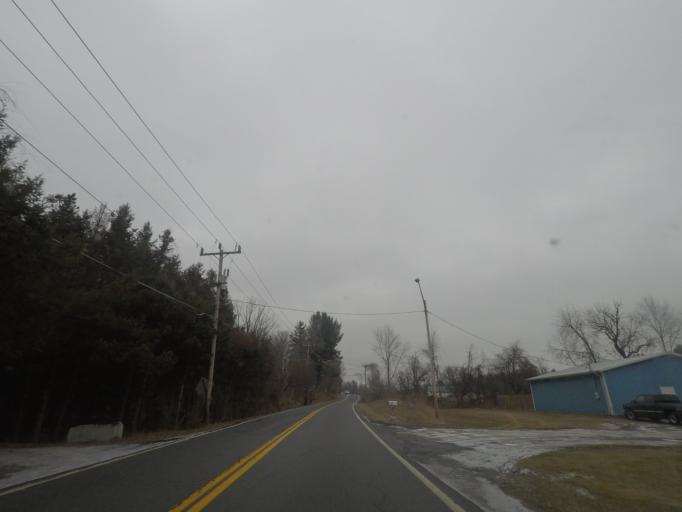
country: US
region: New York
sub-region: Saratoga County
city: Country Knolls
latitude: 42.9158
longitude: -73.7563
